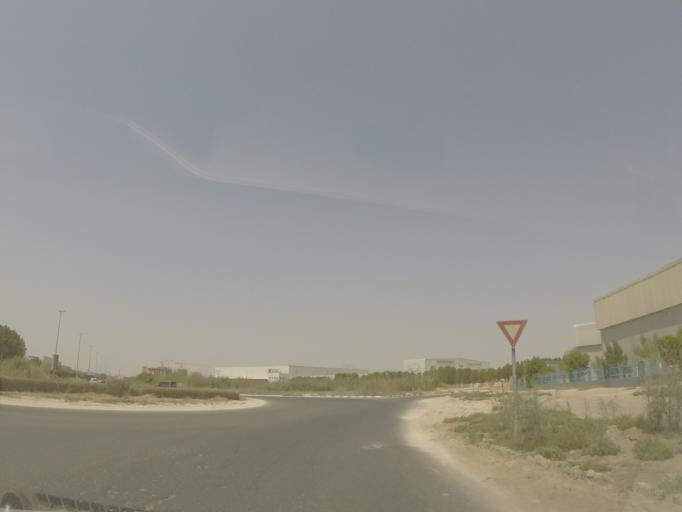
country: AE
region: Dubai
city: Dubai
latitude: 24.9856
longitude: 55.1921
